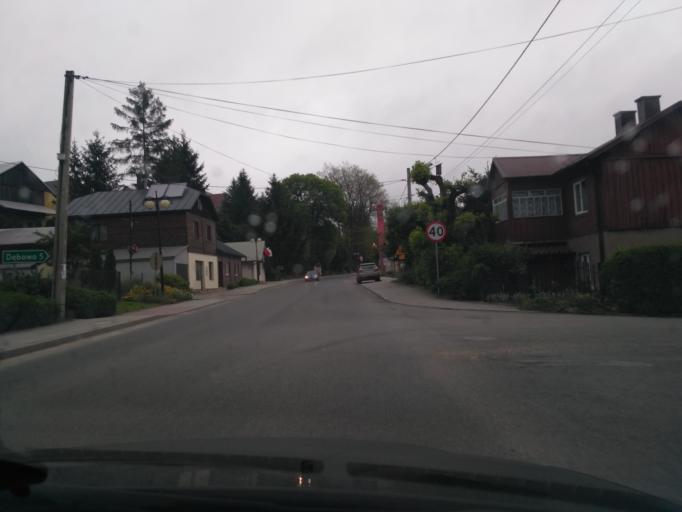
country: PL
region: Subcarpathian Voivodeship
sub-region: Powiat debicki
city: Jodlowa
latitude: 49.8774
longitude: 21.3075
